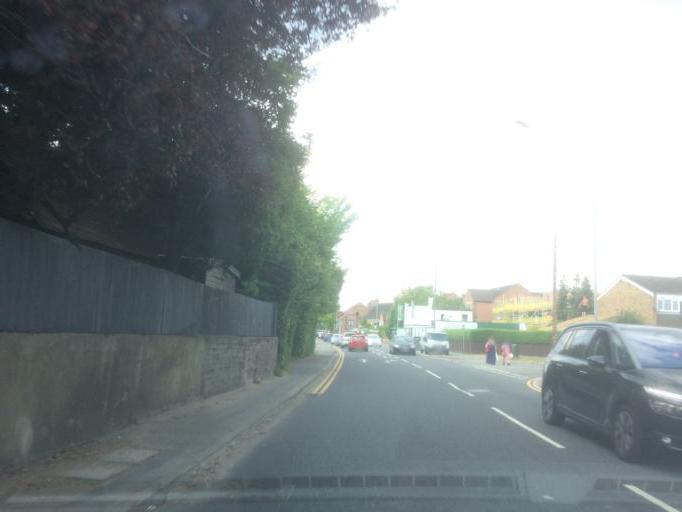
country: GB
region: England
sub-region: Buckinghamshire
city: Farnham Royal
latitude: 51.5528
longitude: -0.6155
